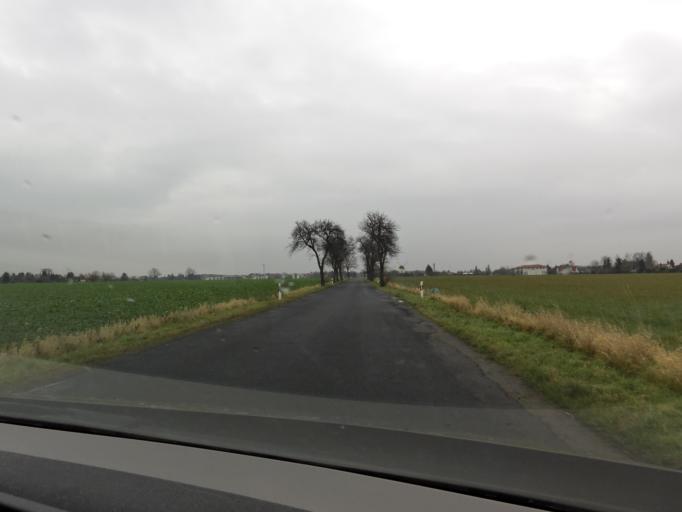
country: DE
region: Saxony
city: Zwenkau
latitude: 51.2745
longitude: 12.2929
